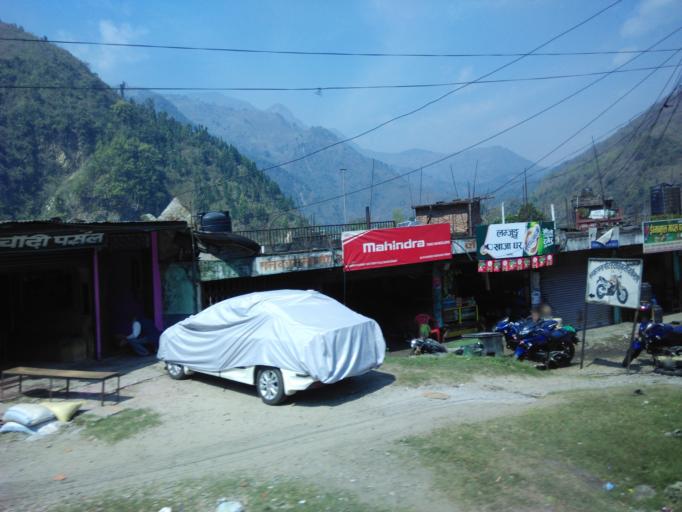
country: NP
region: Central Region
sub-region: Narayani Zone
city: Bharatpur
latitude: 27.8553
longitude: 84.5601
